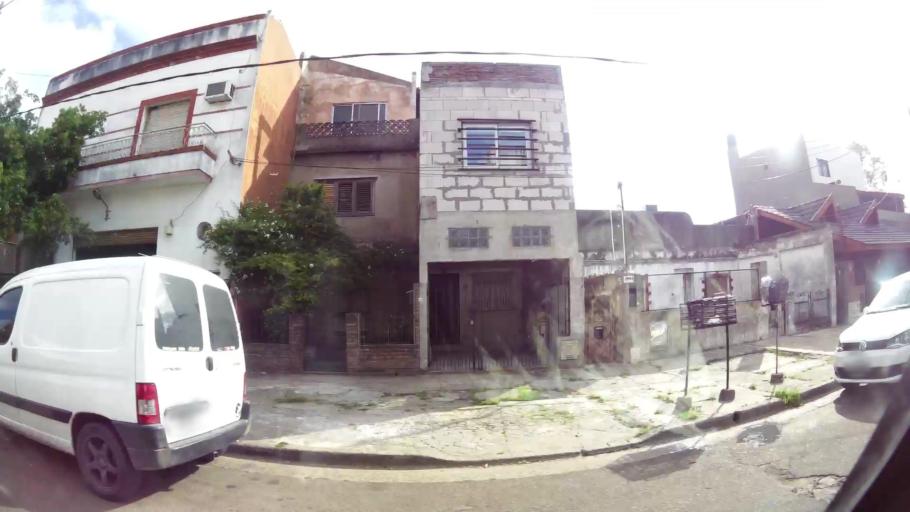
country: AR
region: Buenos Aires
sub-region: Partido de Lanus
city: Lanus
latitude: -34.6940
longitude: -58.3723
